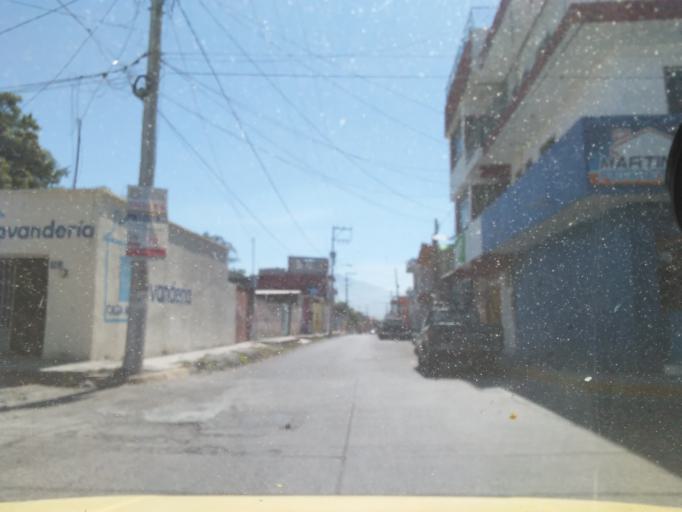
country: MX
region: Nayarit
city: Xalisco
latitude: 21.4486
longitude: -104.8982
